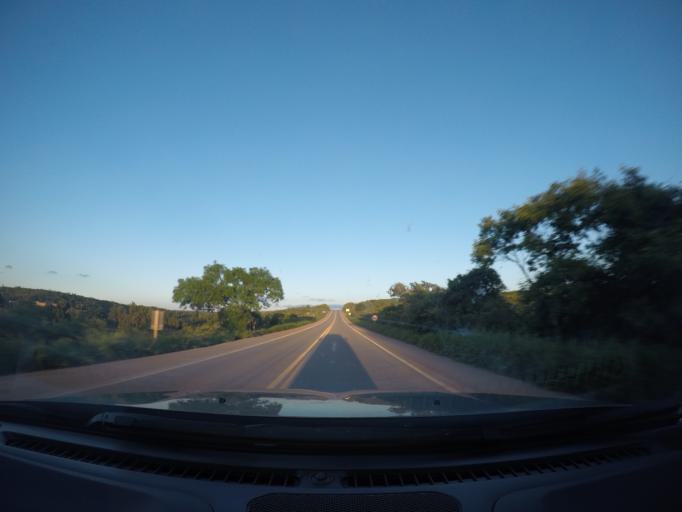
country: BR
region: Bahia
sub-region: Seabra
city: Seabra
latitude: -12.3962
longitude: -41.9329
